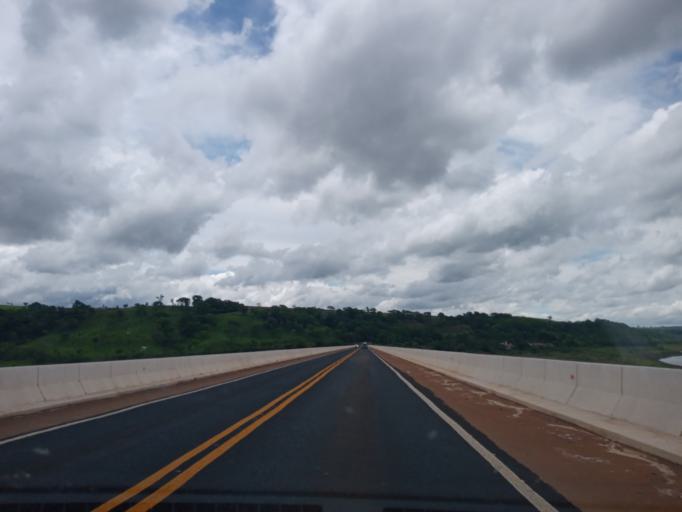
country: BR
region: Minas Gerais
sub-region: Monte Carmelo
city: Monte Carmelo
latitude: -19.2690
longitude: -47.6365
